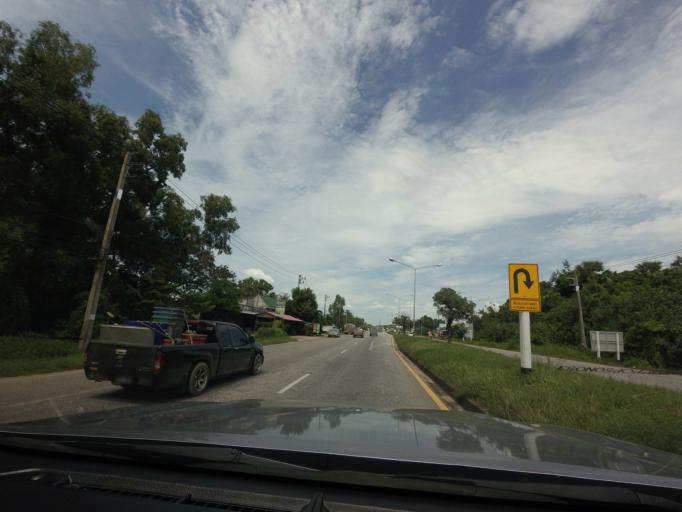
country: TH
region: Songkhla
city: Singhanakhon
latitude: 7.2463
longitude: 100.5399
